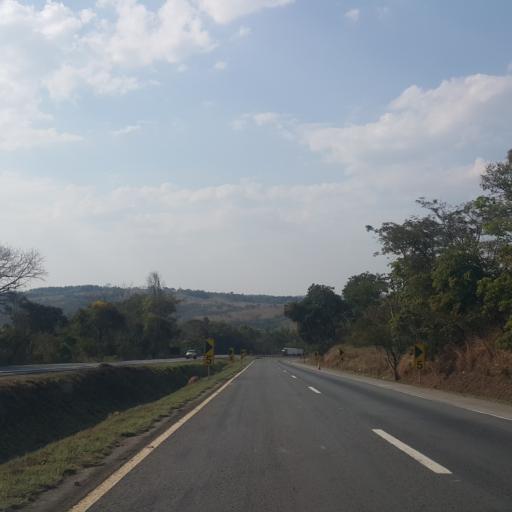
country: BR
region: Goias
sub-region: Abadiania
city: Abadiania
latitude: -16.1527
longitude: -48.6109
